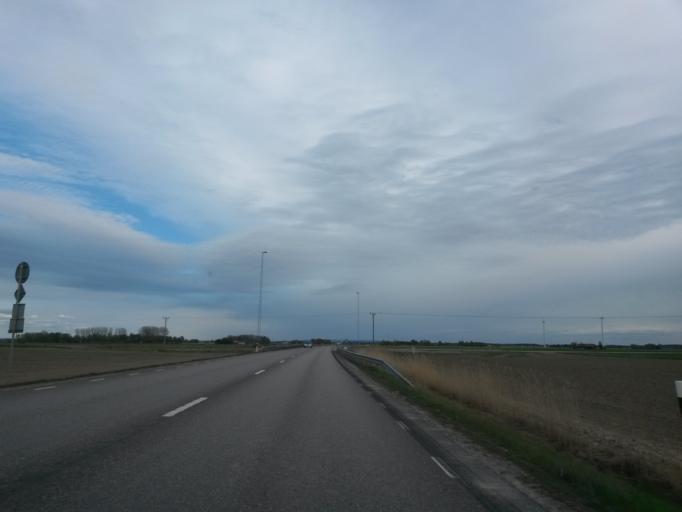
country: SE
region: Vaestra Goetaland
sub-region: Vara Kommun
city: Vara
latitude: 58.2952
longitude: 12.9585
